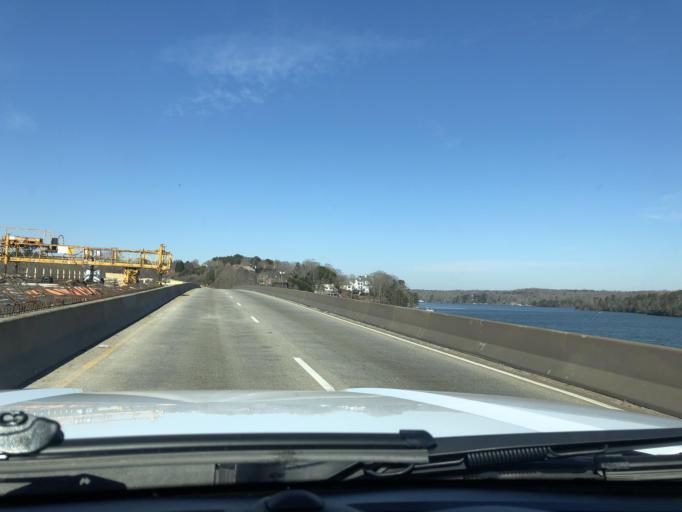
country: US
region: Georgia
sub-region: Hall County
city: Gainesville
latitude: 34.3213
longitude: -83.8789
